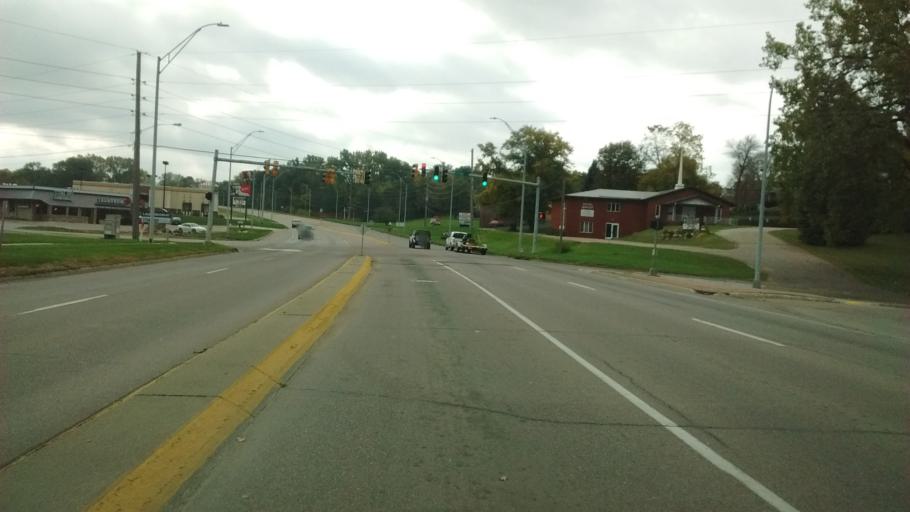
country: US
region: Iowa
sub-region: Woodbury County
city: Sioux City
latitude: 42.4797
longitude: -96.3524
